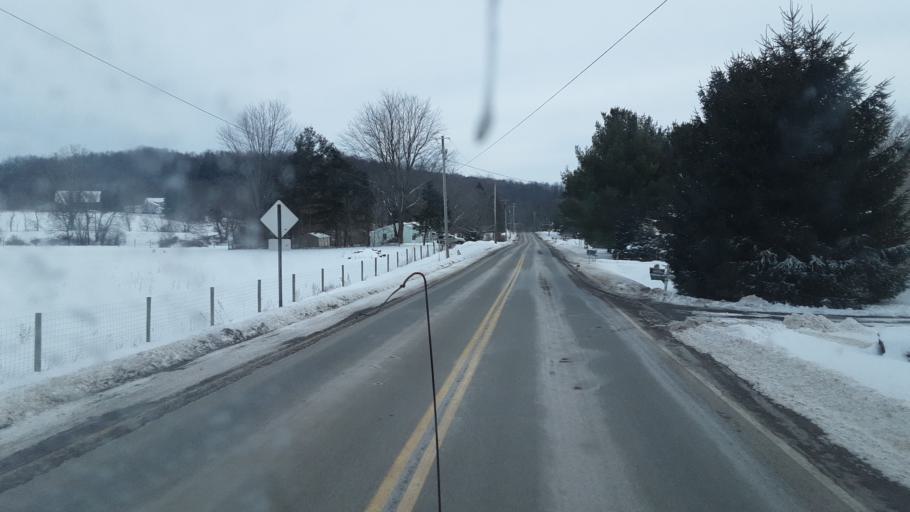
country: US
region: New York
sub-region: Wayne County
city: Lyons
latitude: 43.0898
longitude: -77.0463
